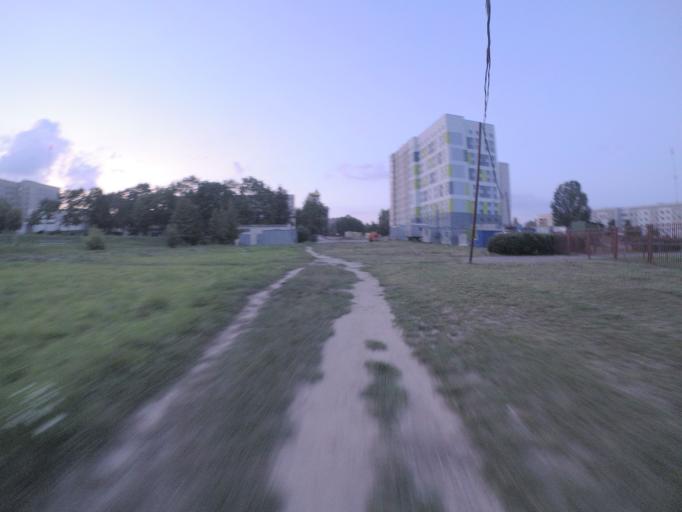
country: BY
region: Grodnenskaya
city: Hrodna
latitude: 53.7022
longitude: 23.8107
